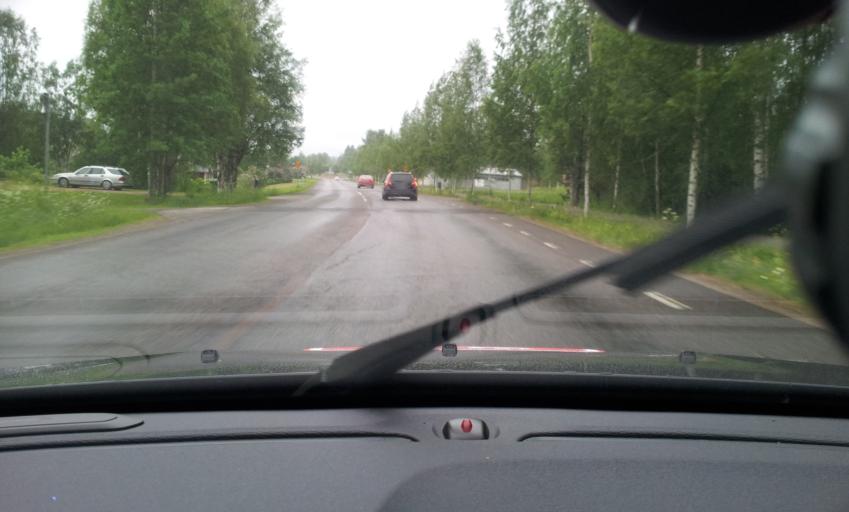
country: SE
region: Jaemtland
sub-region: Ragunda Kommun
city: Hammarstrand
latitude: 63.0205
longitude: 16.6436
